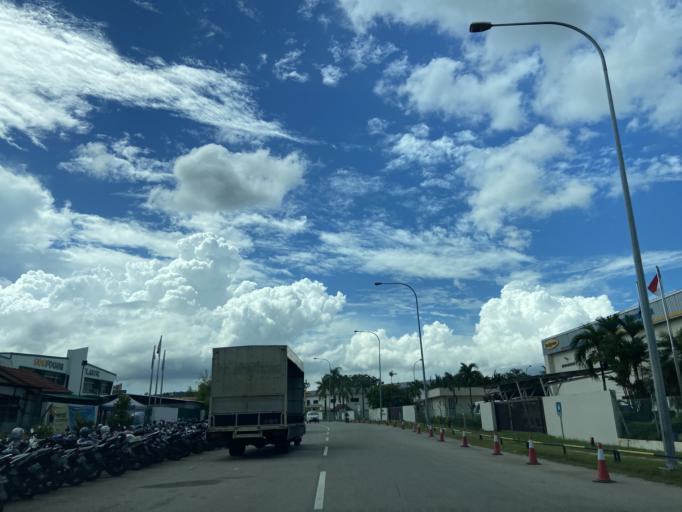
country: SG
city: Singapore
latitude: 1.0606
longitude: 104.0326
